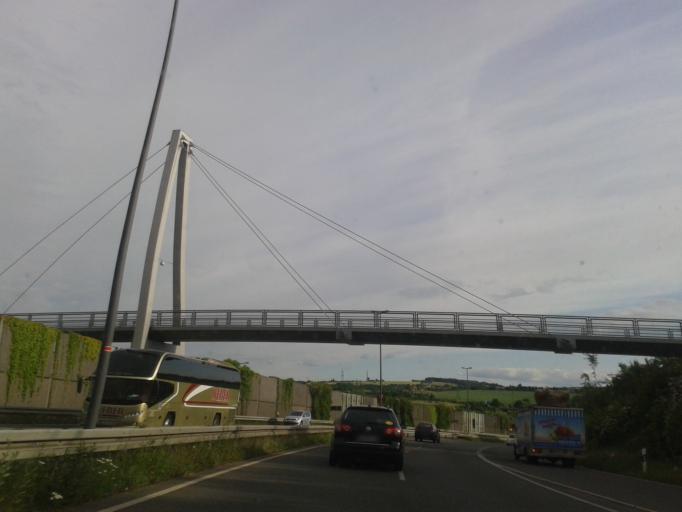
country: DE
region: Saxony
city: Bannewitz
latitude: 51.0178
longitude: 13.7293
